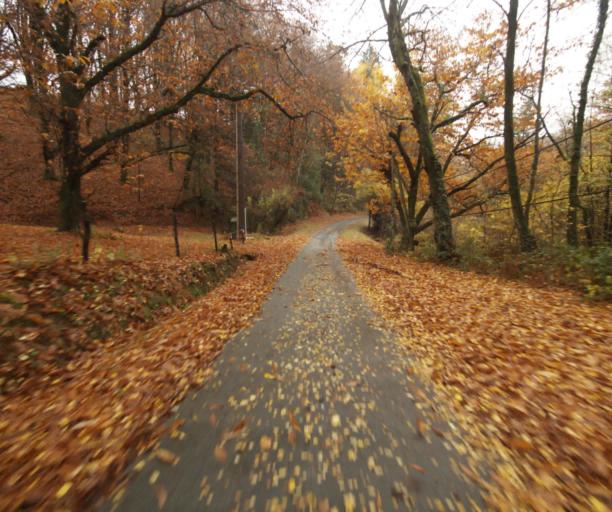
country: FR
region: Limousin
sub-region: Departement de la Correze
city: Cornil
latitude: 45.1890
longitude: 1.6360
